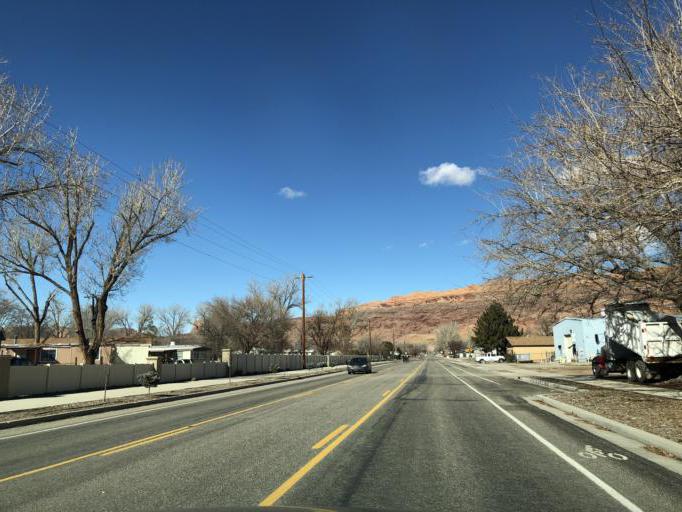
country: US
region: Utah
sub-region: Grand County
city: Moab
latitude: 38.5774
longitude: -109.5612
